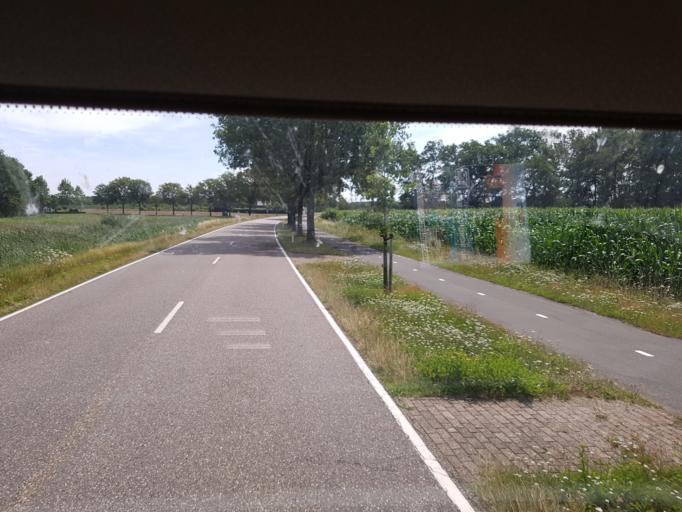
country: NL
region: Limburg
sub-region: Gemeente Nederweert
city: Nederweert
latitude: 51.2648
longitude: 5.7835
